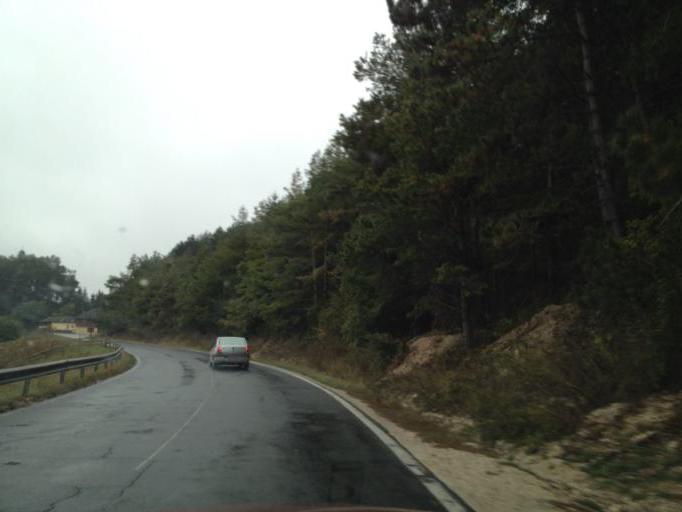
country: RO
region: Arges
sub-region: Comuna Valea Mare-Pravat
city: Valea Mare Pravat
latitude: 45.2949
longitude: 25.1412
